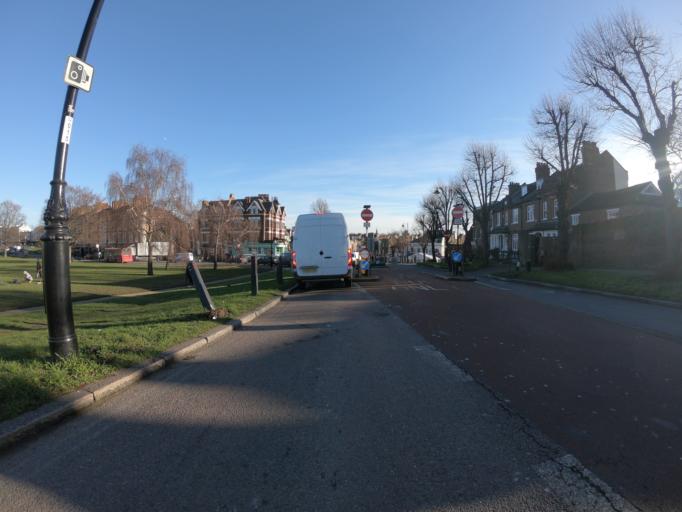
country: GB
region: England
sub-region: Greater London
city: Blackheath
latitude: 51.4673
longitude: 0.0062
